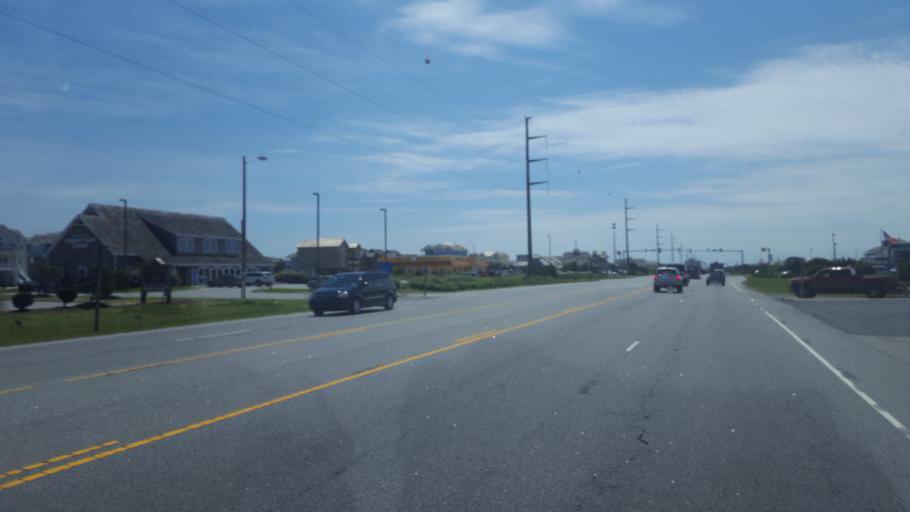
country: US
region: North Carolina
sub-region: Dare County
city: Nags Head
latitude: 35.9397
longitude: -75.6164
